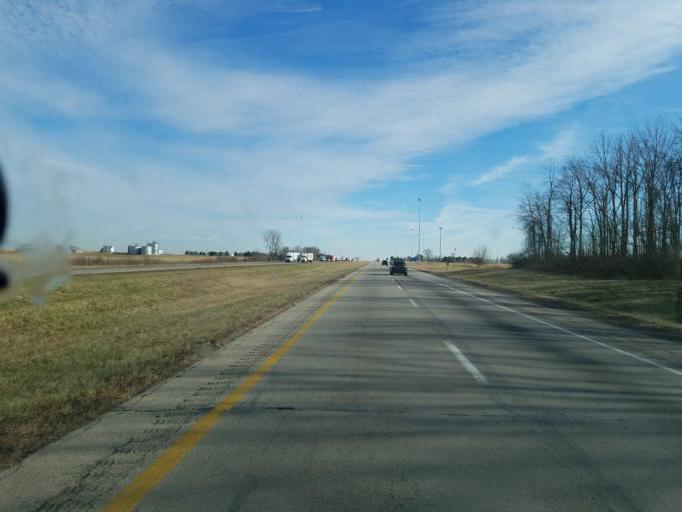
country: US
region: Ohio
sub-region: Preble County
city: New Paris
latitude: 39.8285
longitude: -84.7714
